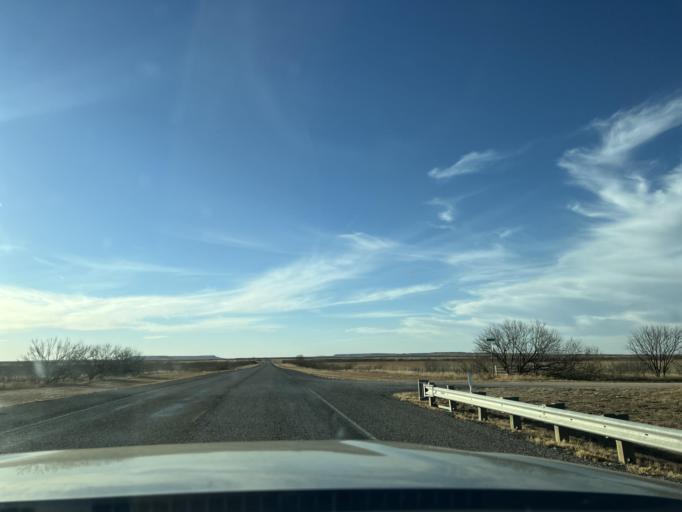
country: US
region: Texas
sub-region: Borden County
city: Gail
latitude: 32.7702
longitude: -101.3282
